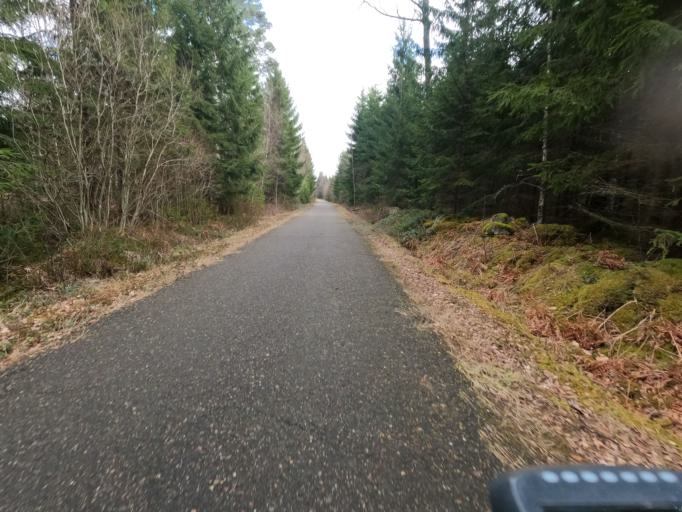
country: SE
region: Joenkoeping
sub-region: Varnamo Kommun
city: Rydaholm
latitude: 56.8531
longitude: 14.1905
